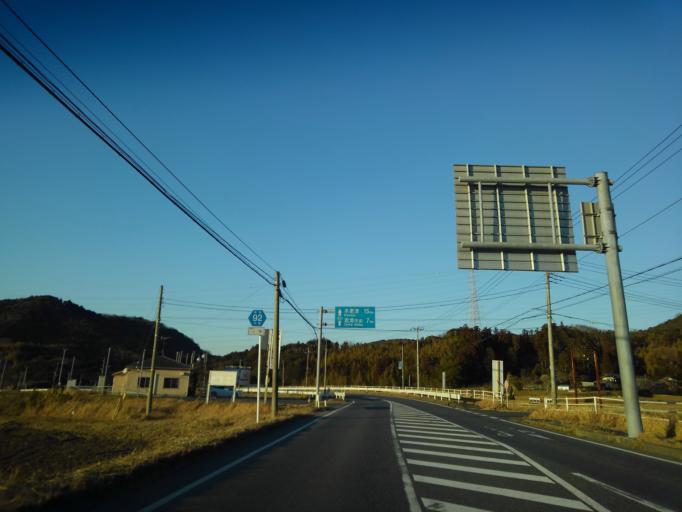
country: JP
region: Chiba
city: Kisarazu
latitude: 35.3033
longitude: 139.9871
